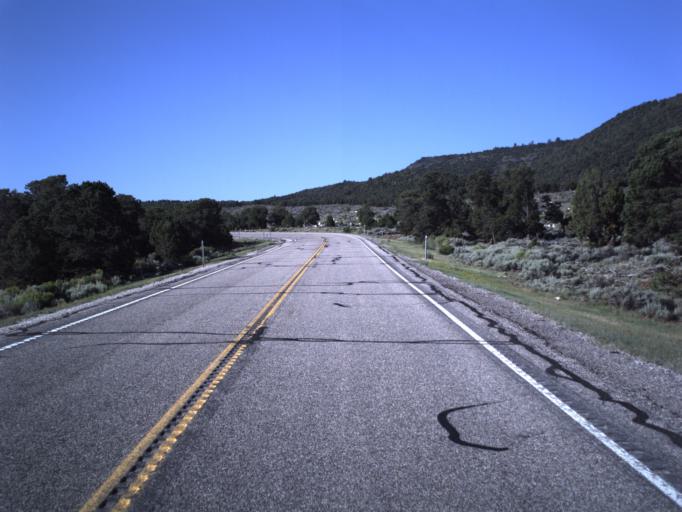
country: US
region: Utah
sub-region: Wayne County
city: Loa
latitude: 38.7056
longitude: -111.4017
